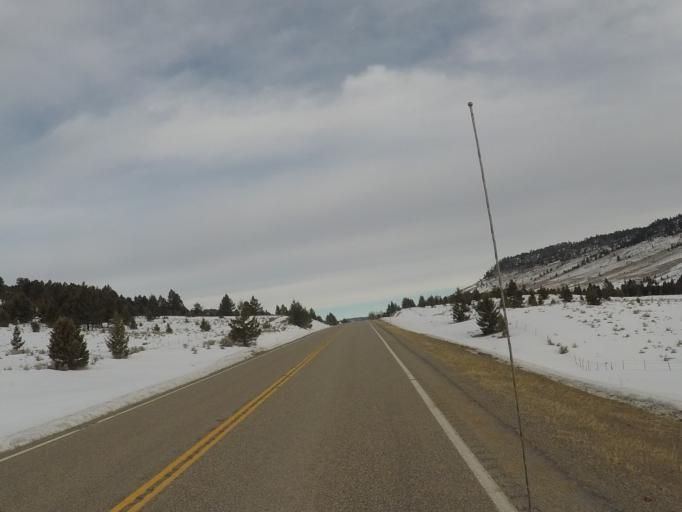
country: US
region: Montana
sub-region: Meagher County
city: White Sulphur Springs
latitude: 46.6343
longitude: -110.8541
